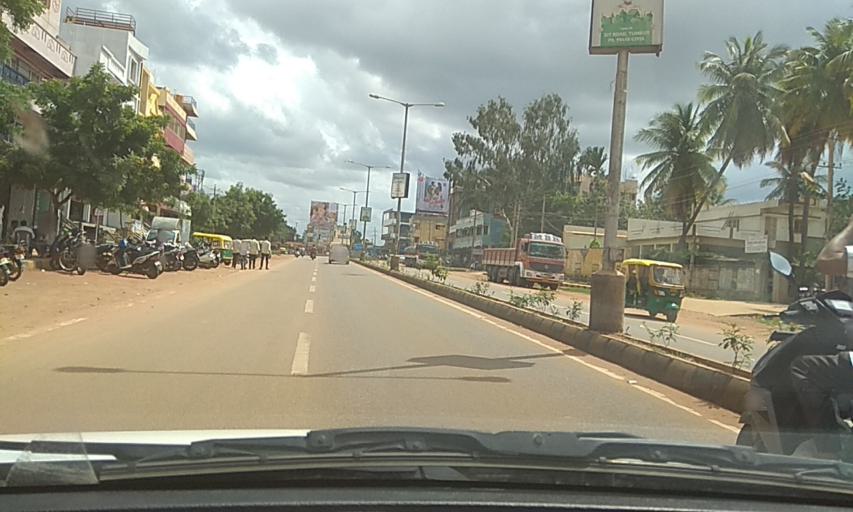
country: IN
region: Karnataka
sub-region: Tumkur
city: Tumkur
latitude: 13.3262
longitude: 77.0935
